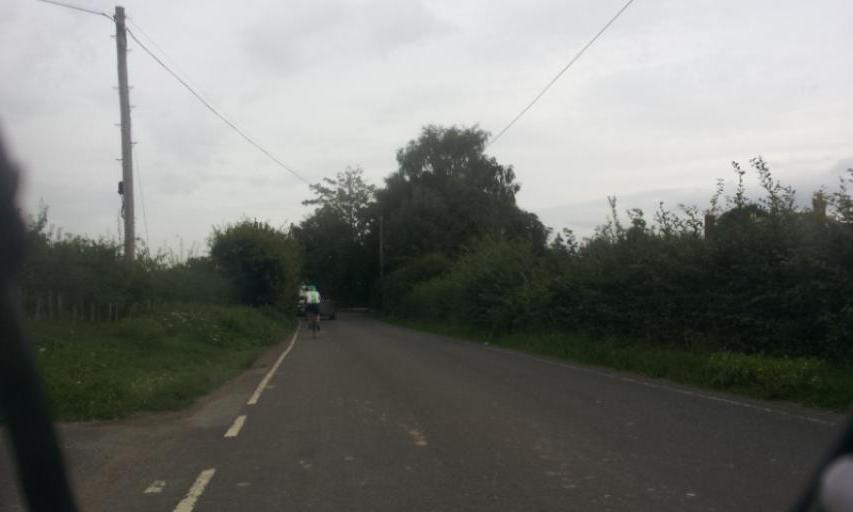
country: GB
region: England
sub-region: Kent
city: Hadlow
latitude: 51.2081
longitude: 0.3393
